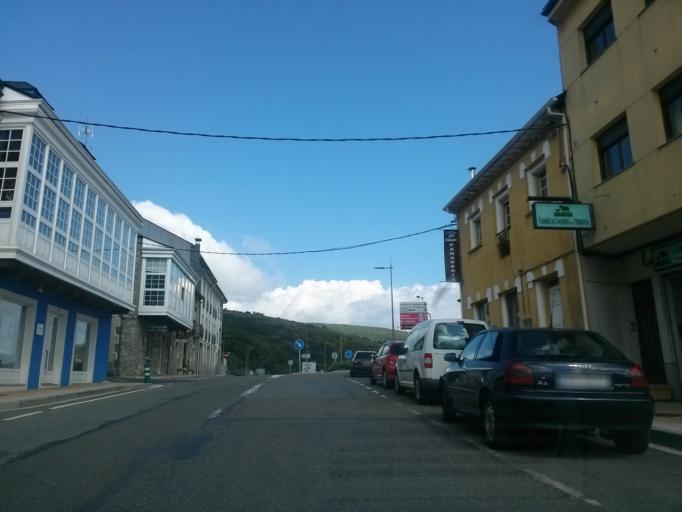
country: ES
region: Castille and Leon
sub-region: Provincia de Leon
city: Balboa
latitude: 42.7264
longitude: -7.0210
